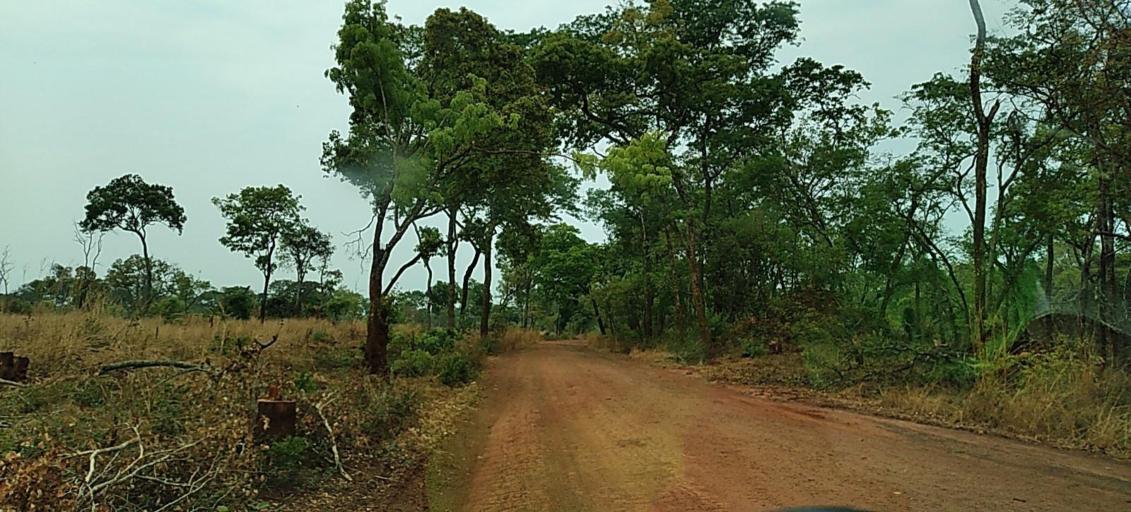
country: ZM
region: North-Western
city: Solwezi
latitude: -12.3175
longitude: 26.5223
